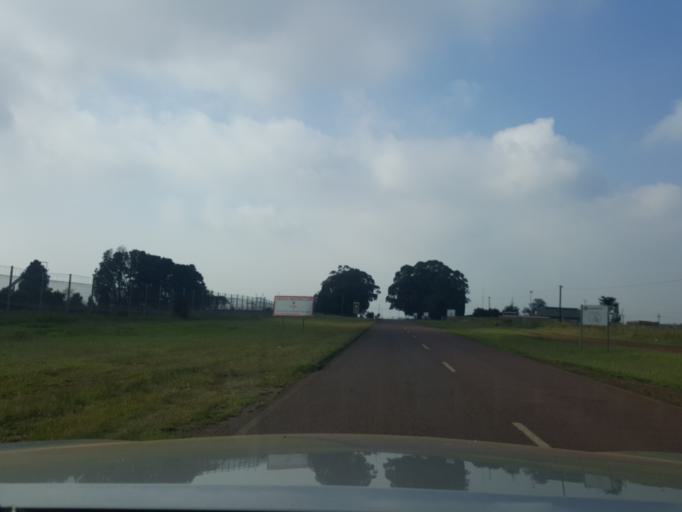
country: ZA
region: Mpumalanga
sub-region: Nkangala District Municipality
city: Middelburg
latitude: -25.9768
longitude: 29.4511
